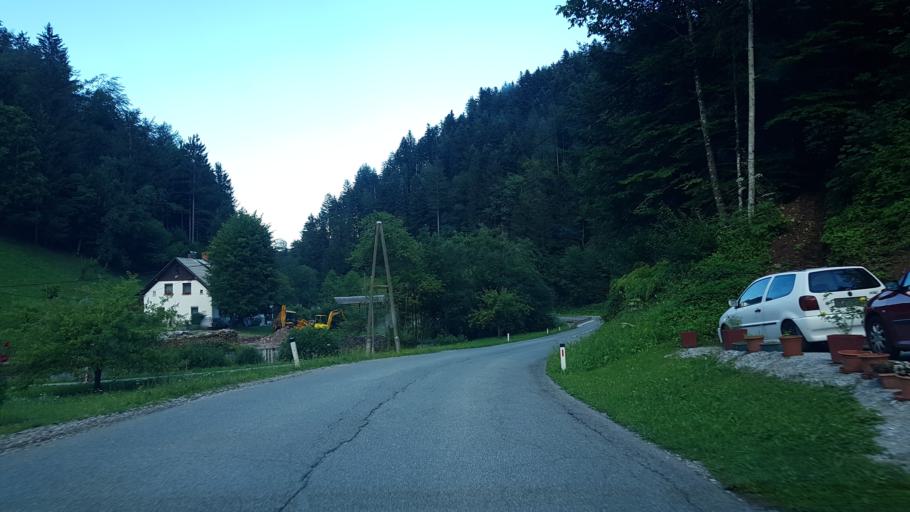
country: SI
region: Idrija
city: Spodnja Idrija
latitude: 46.0823
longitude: 14.0568
